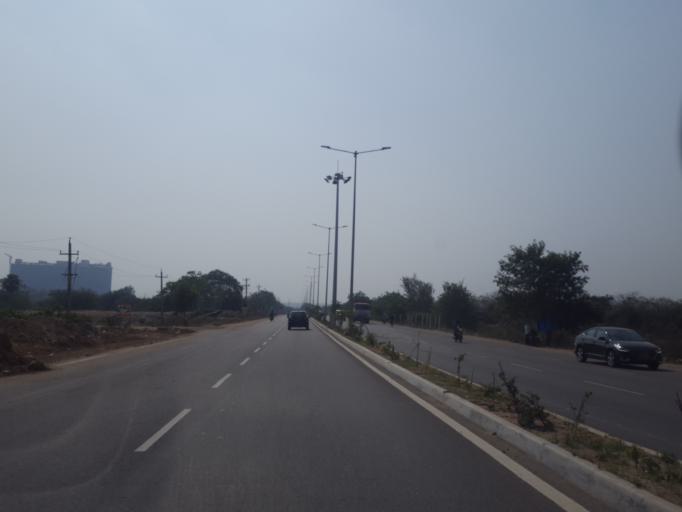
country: IN
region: Telangana
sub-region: Medak
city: Serilingampalle
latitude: 17.4147
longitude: 78.3335
